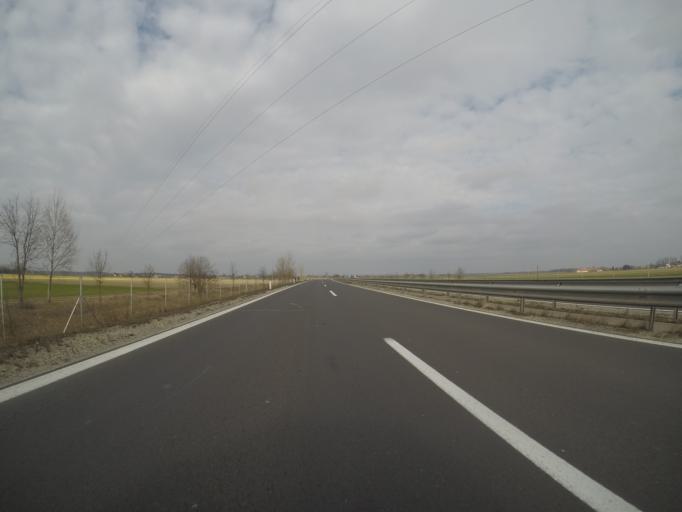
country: SI
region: Murska Sobota
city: Bakovci
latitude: 46.6217
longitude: 16.1337
